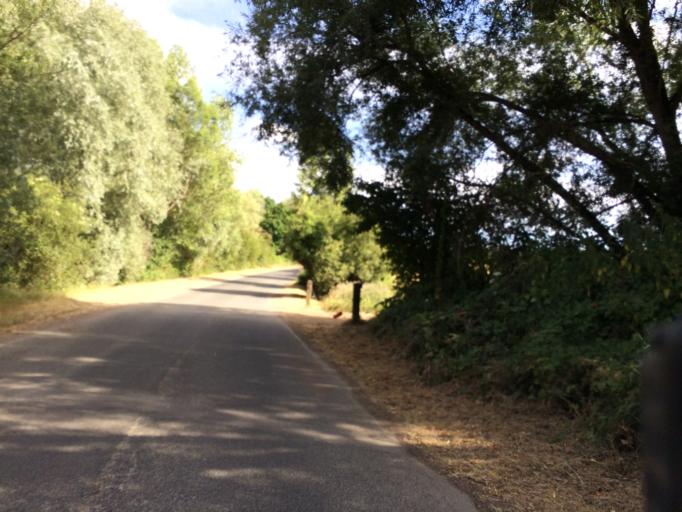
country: FR
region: Ile-de-France
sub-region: Departement de l'Essonne
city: Tigery
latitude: 48.6438
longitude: 2.5001
